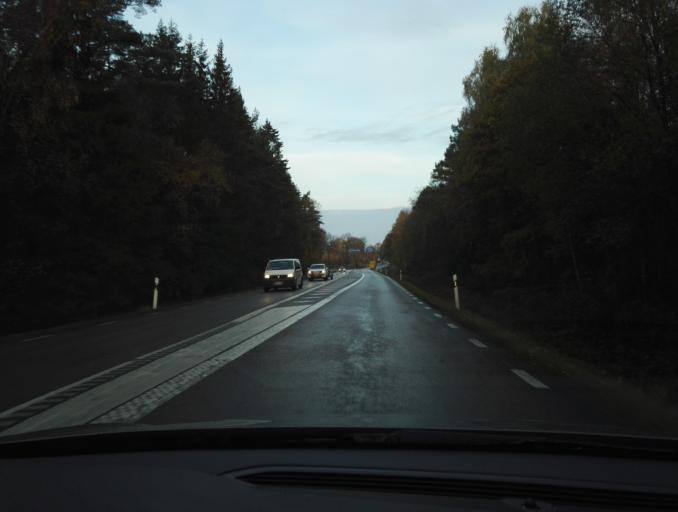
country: SE
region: Kronoberg
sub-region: Alvesta Kommun
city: Moheda
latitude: 56.9925
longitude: 14.6810
